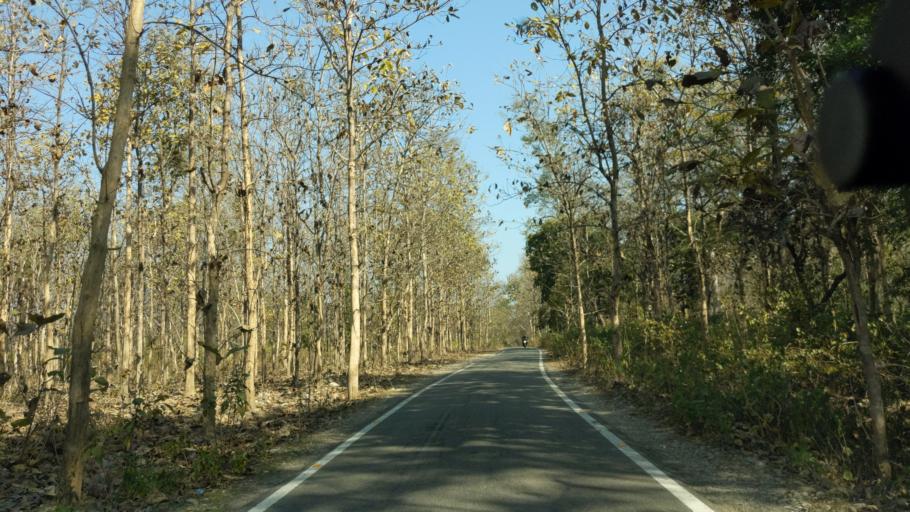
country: IN
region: Uttarakhand
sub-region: Naini Tal
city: Ramnagar
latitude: 29.4272
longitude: 79.1399
